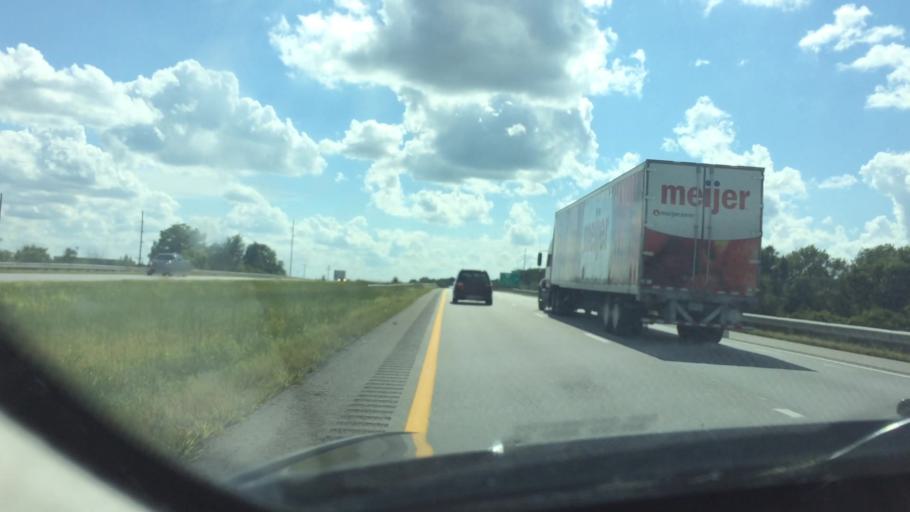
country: US
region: Ohio
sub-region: Shelby County
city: Sidney
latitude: 40.3186
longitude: -84.1687
